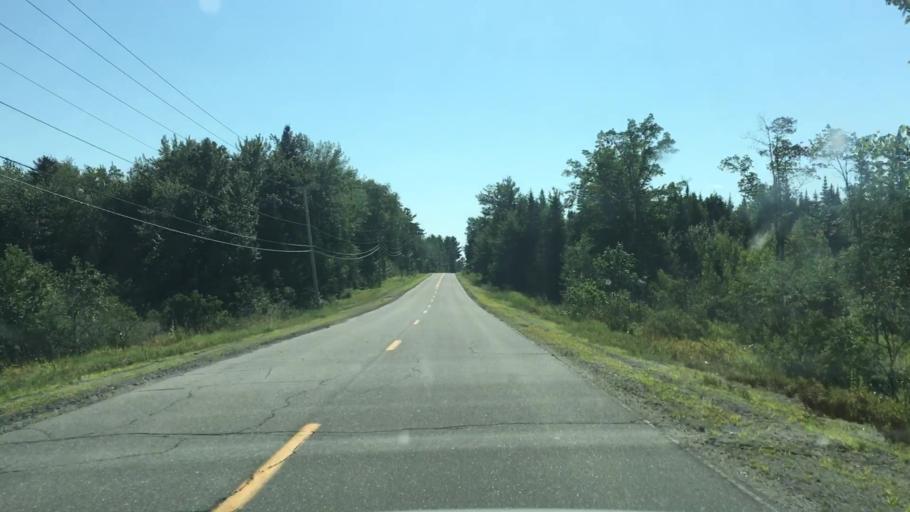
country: US
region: Maine
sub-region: Penobscot County
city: Enfield
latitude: 45.2441
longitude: -68.6137
